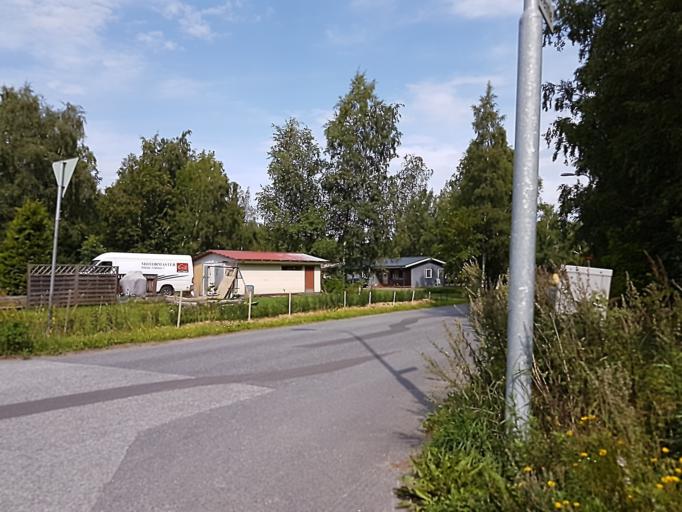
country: FI
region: Pirkanmaa
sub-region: Etelae-Pirkanmaa
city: Valkeakoski
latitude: 61.2507
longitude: 24.0538
